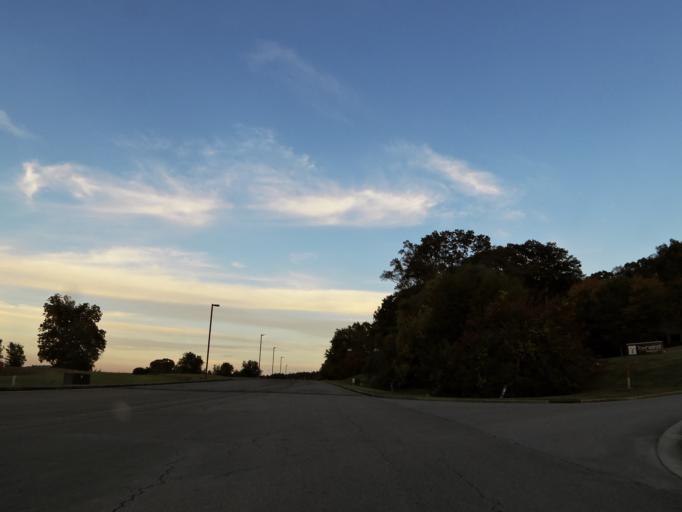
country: US
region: Tennessee
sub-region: Blount County
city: Eagleton Village
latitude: 35.8619
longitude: -83.9363
